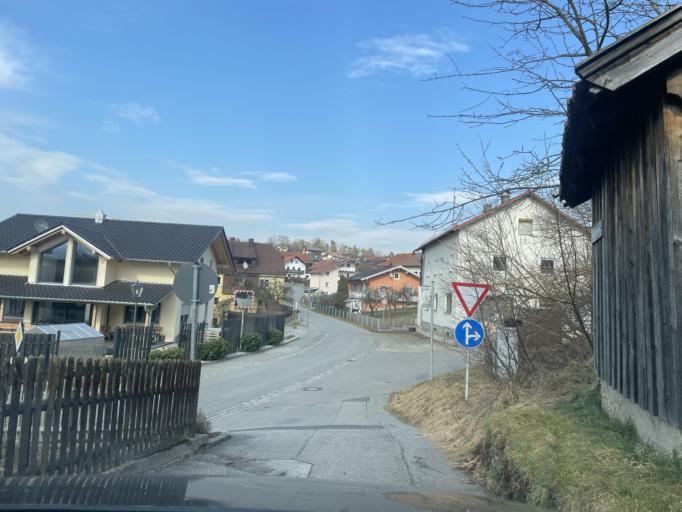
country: DE
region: Bavaria
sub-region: Lower Bavaria
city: Viechtach
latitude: 49.0826
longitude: 12.9017
